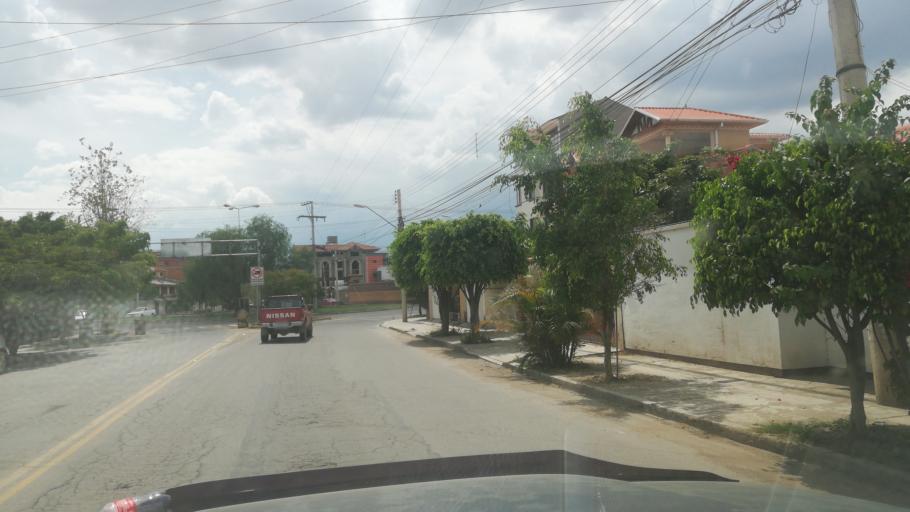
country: BO
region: Cochabamba
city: Cochabamba
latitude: -17.4026
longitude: -66.1791
